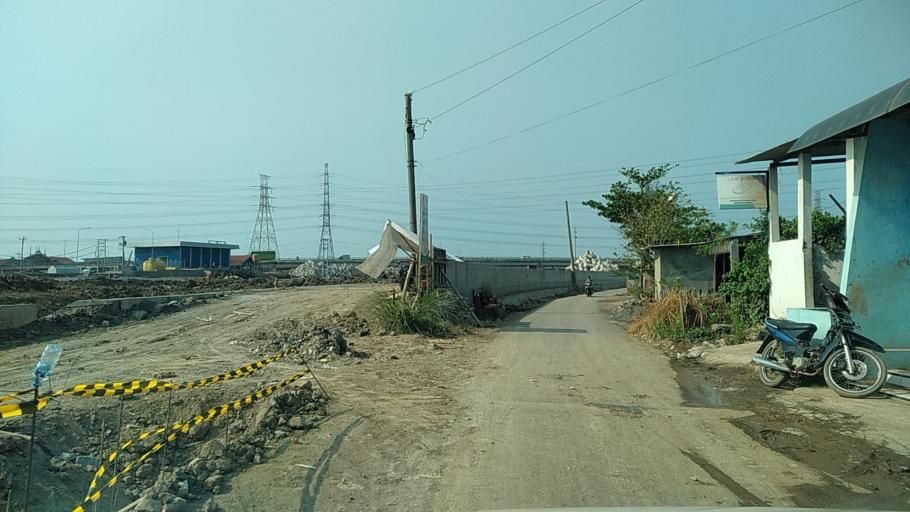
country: ID
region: Central Java
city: Semarang
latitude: -6.9528
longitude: 110.4407
